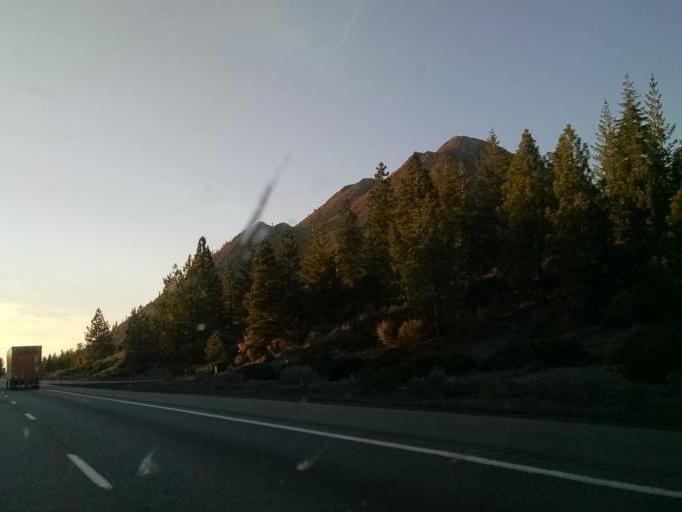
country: US
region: California
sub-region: Siskiyou County
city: Mount Shasta
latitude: 41.3462
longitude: -122.3448
